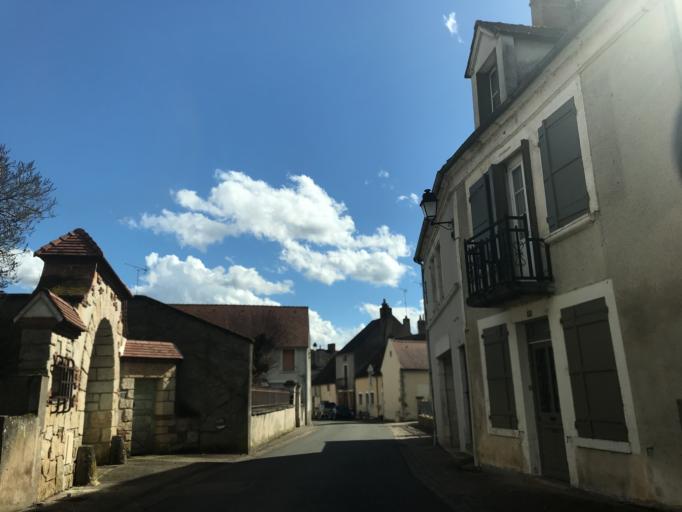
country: FR
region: Bourgogne
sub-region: Departement de la Nievre
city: Clamecy
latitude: 47.5094
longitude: 3.5130
